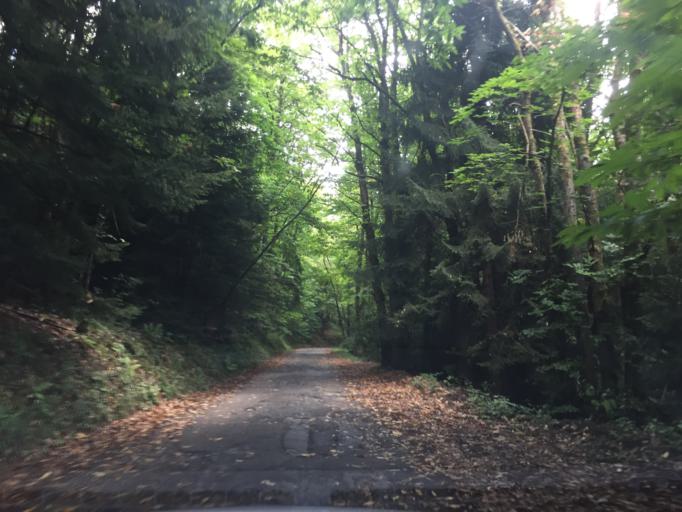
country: FR
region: Rhone-Alpes
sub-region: Departement de la Savoie
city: La Rochette
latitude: 45.4423
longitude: 6.1496
